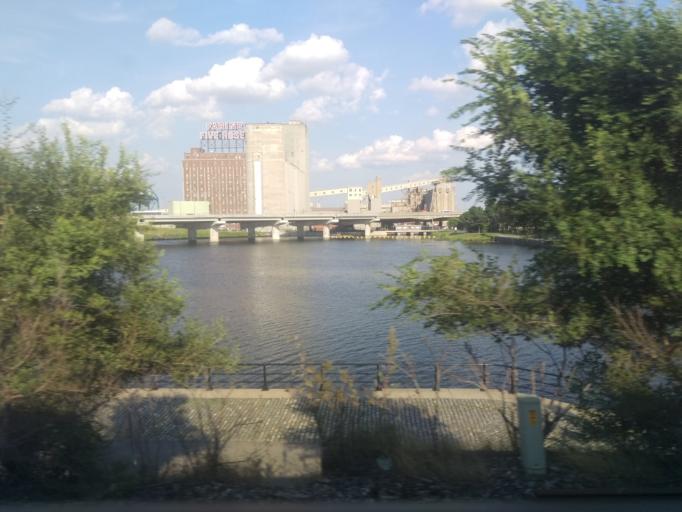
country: CA
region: Quebec
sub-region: Montreal
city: Montreal
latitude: 45.4915
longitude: -73.5561
